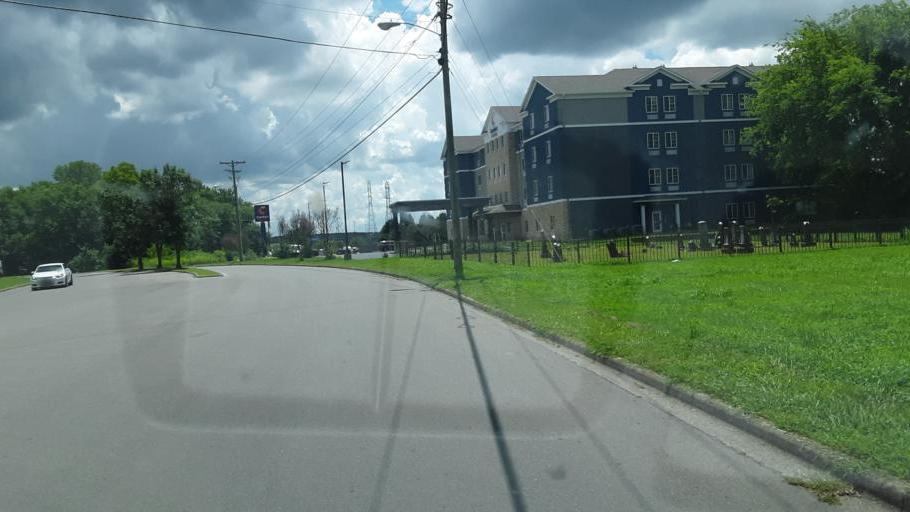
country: US
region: Tennessee
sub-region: Montgomery County
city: Clarksville
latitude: 36.5973
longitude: -87.2896
